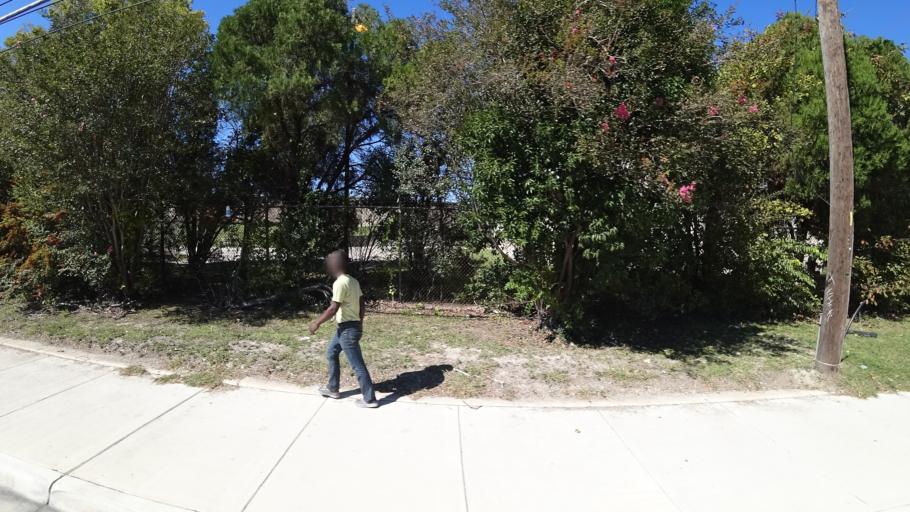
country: US
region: Texas
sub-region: Travis County
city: Austin
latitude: 30.3275
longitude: -97.7254
